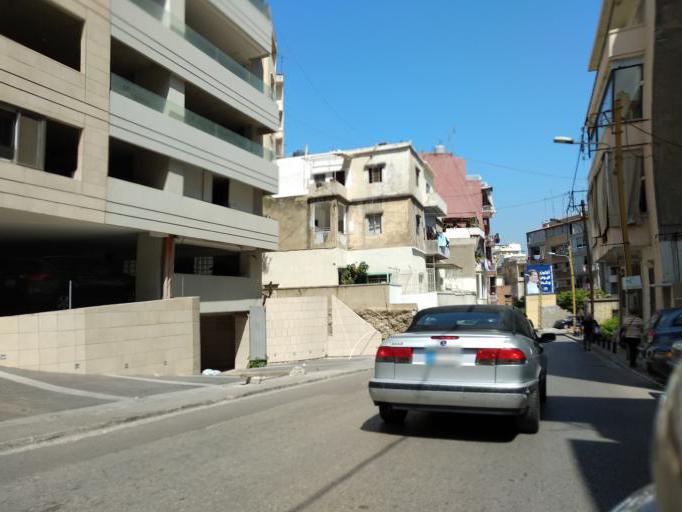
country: LB
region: Mont-Liban
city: Jdaidet el Matn
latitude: 33.8947
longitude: 35.5321
